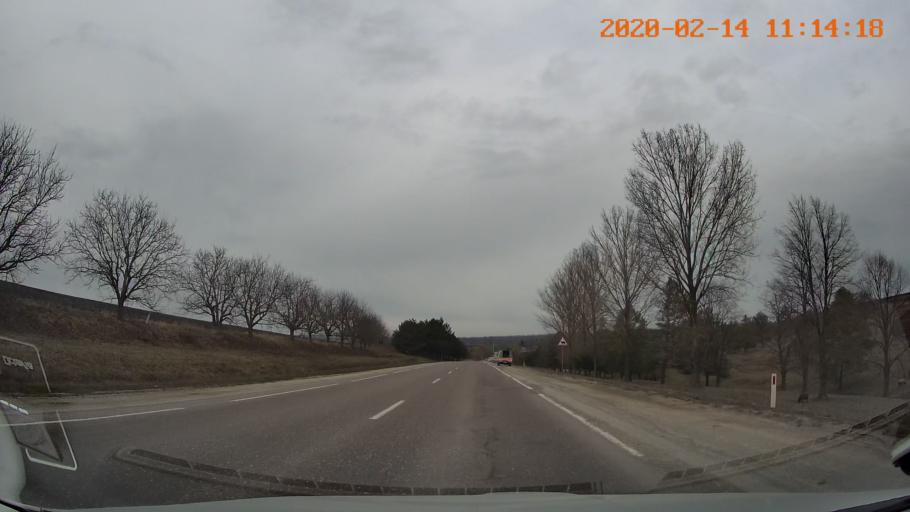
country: MD
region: Raionul Edinet
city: Edinet
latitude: 48.2220
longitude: 27.2235
